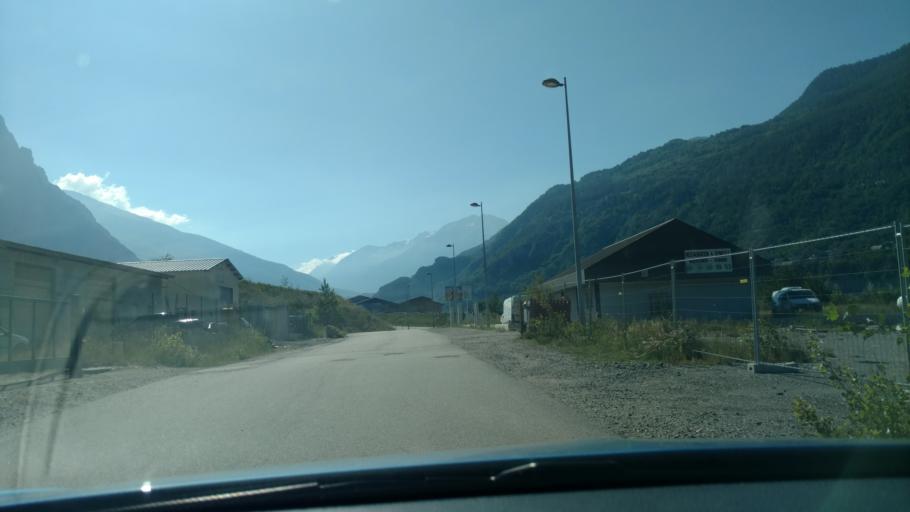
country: FR
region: Rhone-Alpes
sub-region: Departement de la Savoie
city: Villargondran
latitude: 45.2549
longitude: 6.3955
